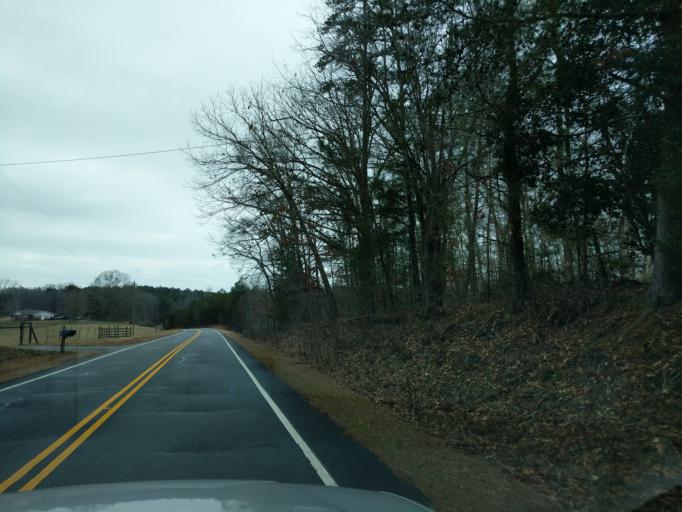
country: US
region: South Carolina
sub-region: Oconee County
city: Walhalla
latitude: 34.7991
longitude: -83.0772
